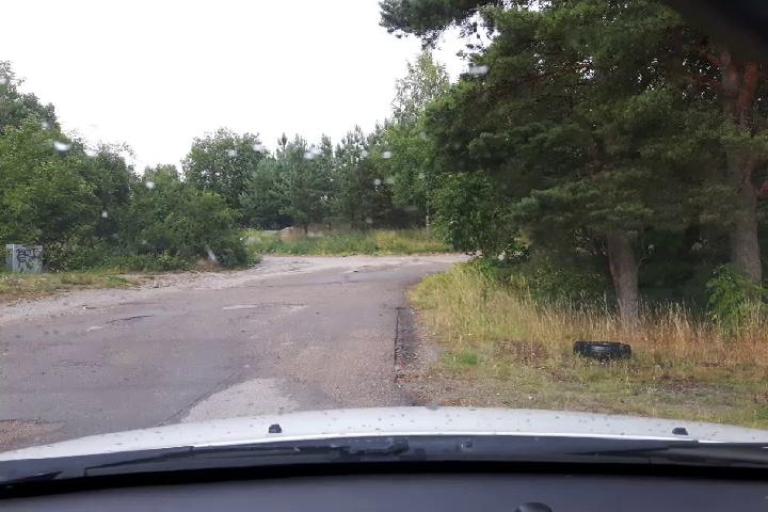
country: SE
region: Uppsala
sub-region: Uppsala Kommun
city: Gamla Uppsala
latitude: 59.9142
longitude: 17.6058
